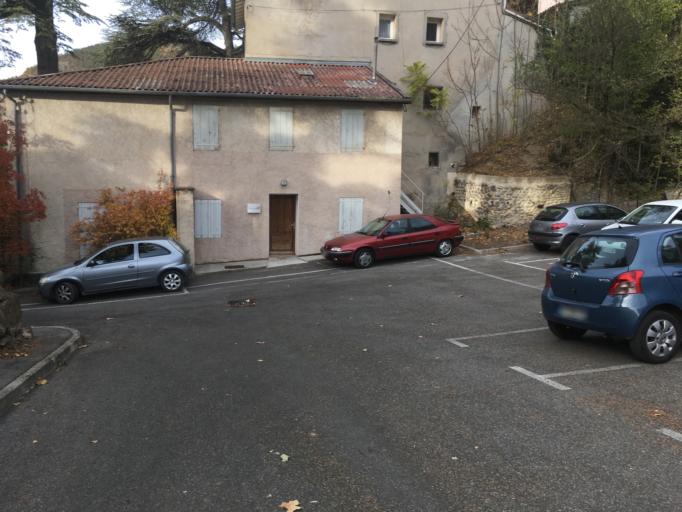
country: FR
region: Provence-Alpes-Cote d'Azur
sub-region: Departement des Alpes-de-Haute-Provence
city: Digne-les-Bains
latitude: 44.0969
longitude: 6.2386
